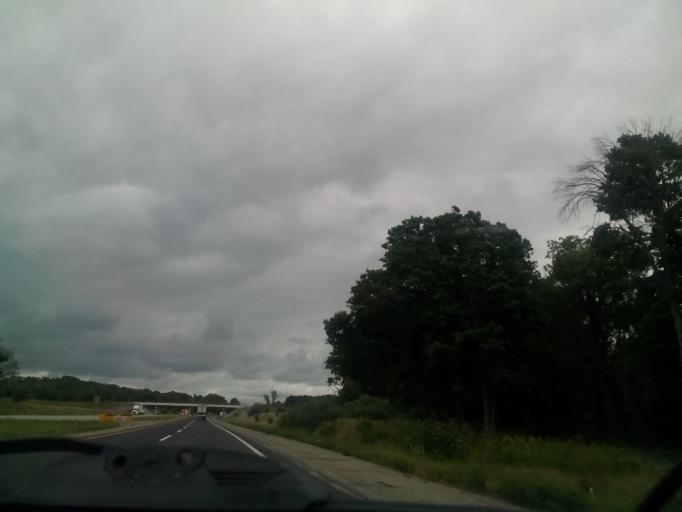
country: US
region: Michigan
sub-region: Branch County
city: Bronson
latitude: 41.7552
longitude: -85.2298
